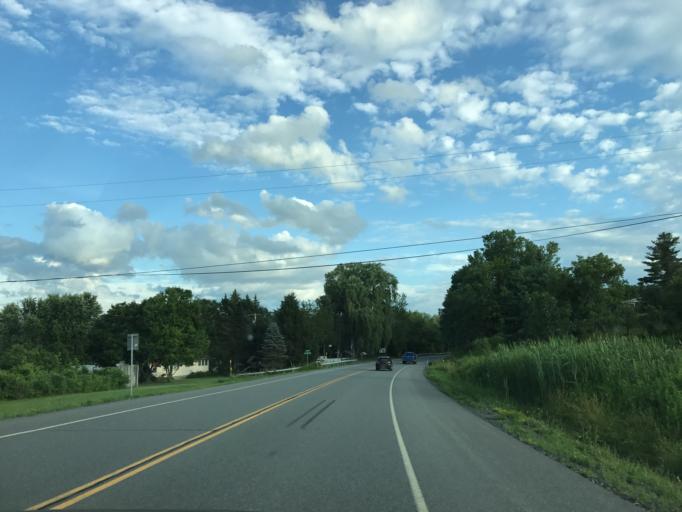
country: US
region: New York
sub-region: Saratoga County
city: Schuylerville
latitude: 43.0510
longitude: -73.5919
